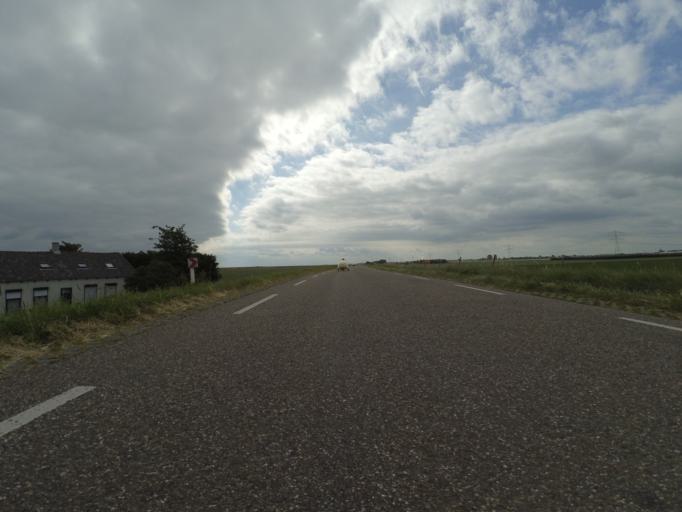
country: NL
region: Zeeland
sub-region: Gemeente Reimerswaal
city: Yerseke
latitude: 51.4609
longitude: 4.0656
